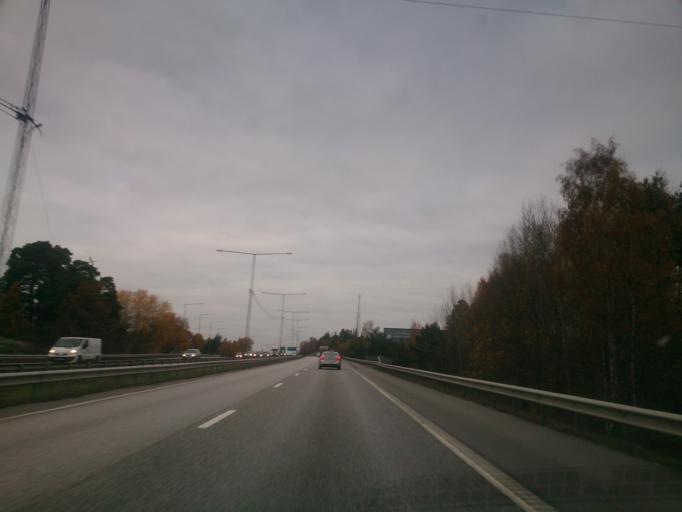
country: SE
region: Stockholm
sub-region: Sodertalje Kommun
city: Pershagen
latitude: 59.1723
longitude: 17.6472
